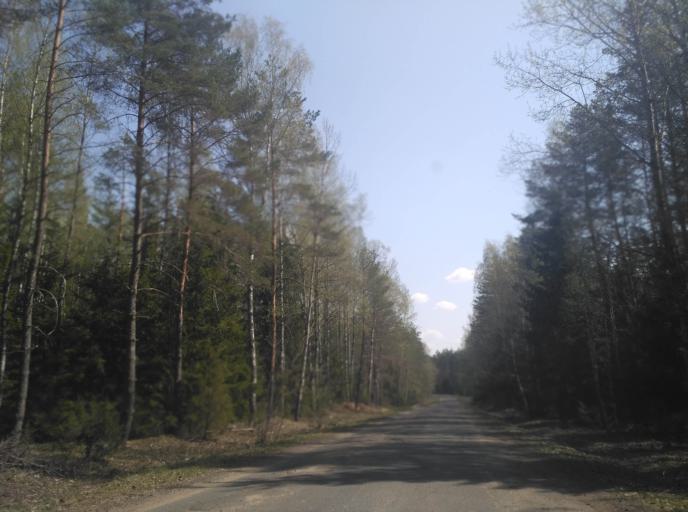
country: BY
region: Minsk
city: Loshnitsa
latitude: 54.4941
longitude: 28.6924
